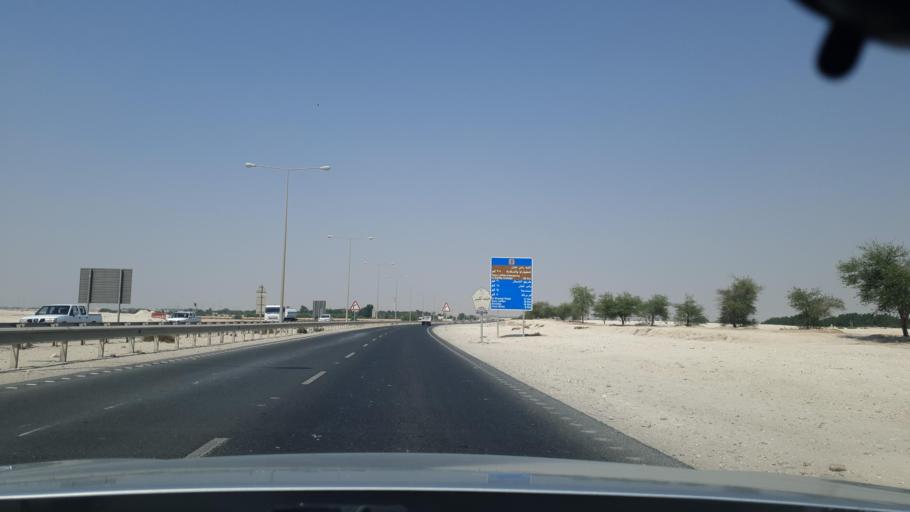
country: QA
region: Al Khawr
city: Al Khawr
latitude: 25.7229
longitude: 51.4987
